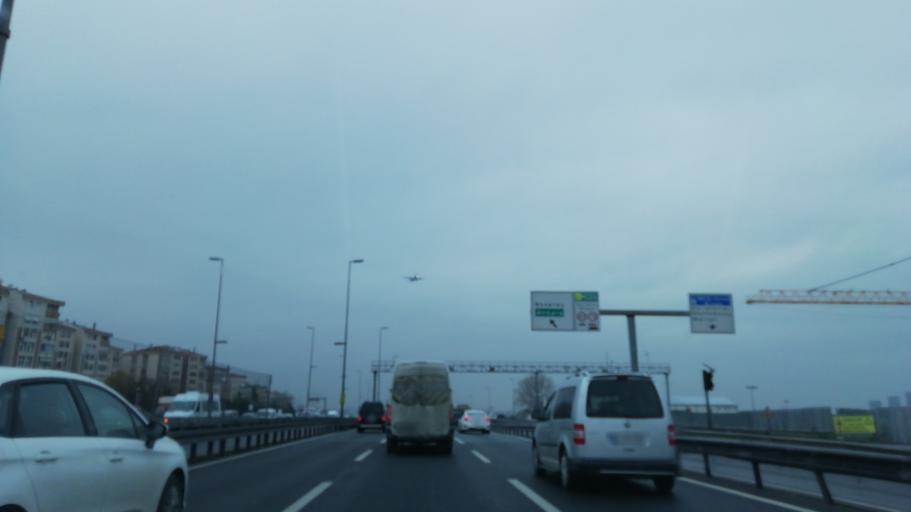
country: TR
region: Istanbul
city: Bahcelievler
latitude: 40.9982
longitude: 28.8740
